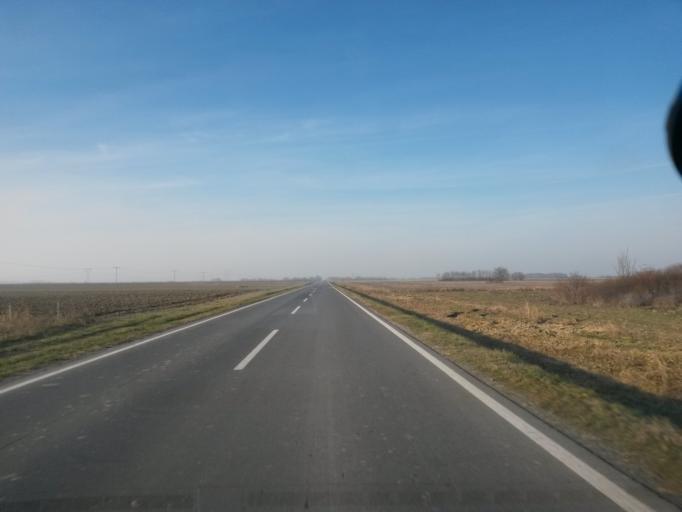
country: HR
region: Osjecko-Baranjska
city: Laslovo
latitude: 45.4225
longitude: 18.6852
